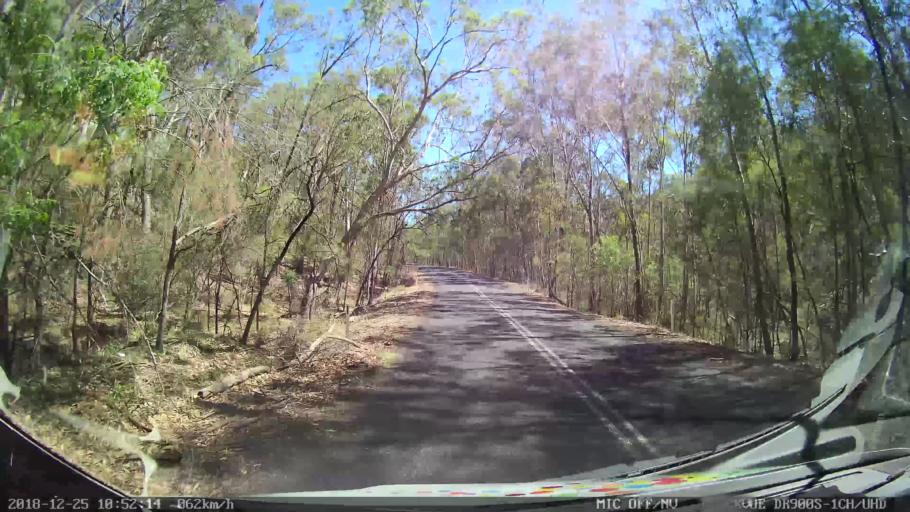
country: AU
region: New South Wales
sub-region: Upper Hunter Shire
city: Merriwa
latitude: -32.4305
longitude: 150.2736
